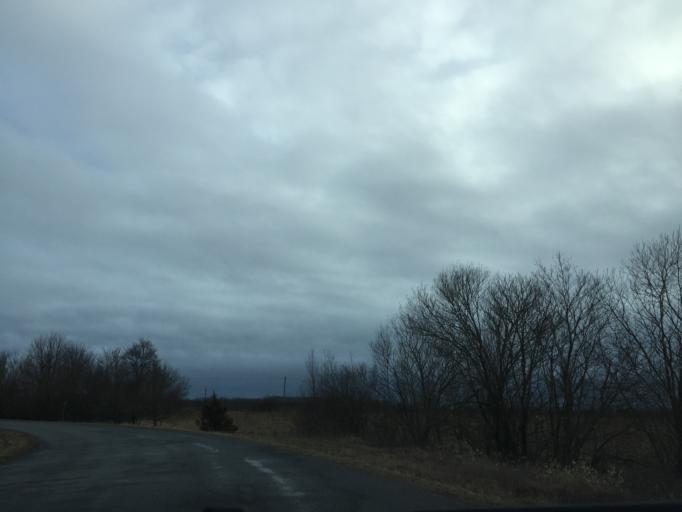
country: EE
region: Laeaene
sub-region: Haapsalu linn
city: Haapsalu
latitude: 58.8090
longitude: 23.5468
